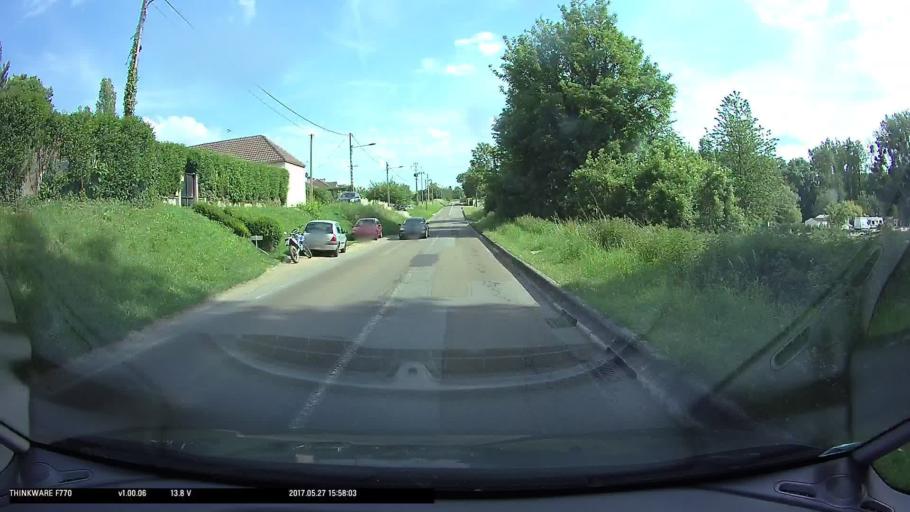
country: FR
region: Ile-de-France
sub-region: Departement du Val-d'Oise
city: Us
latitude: 49.1008
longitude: 1.9753
